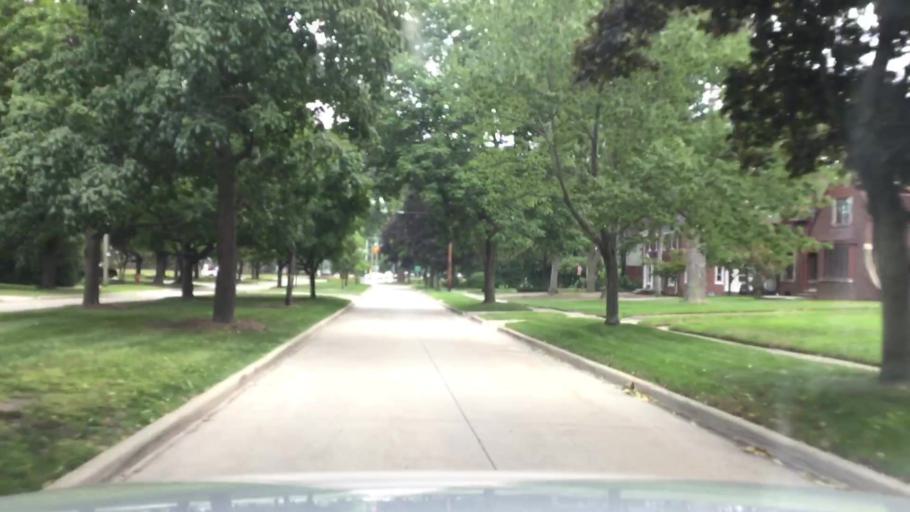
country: US
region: Michigan
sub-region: Oakland County
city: Pleasant Ridge
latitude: 42.4704
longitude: -83.1438
